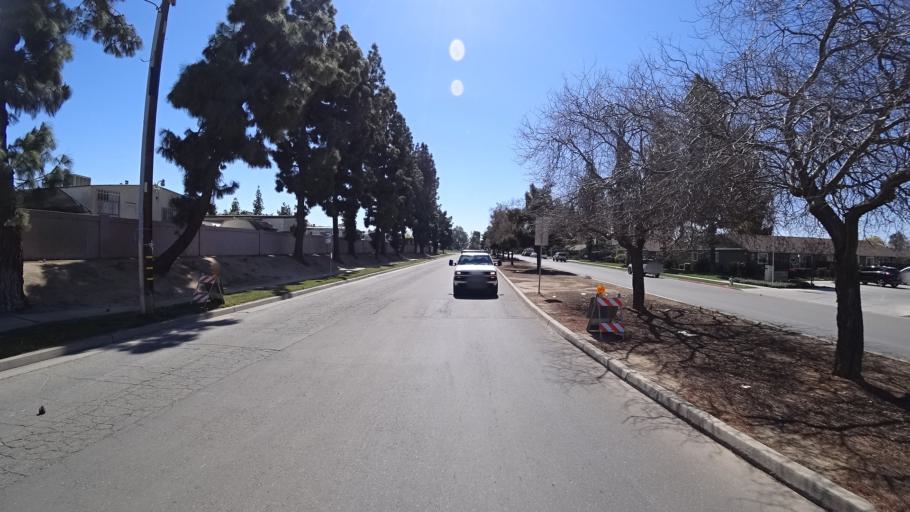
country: US
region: California
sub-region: Fresno County
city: West Park
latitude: 36.7639
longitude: -119.8443
